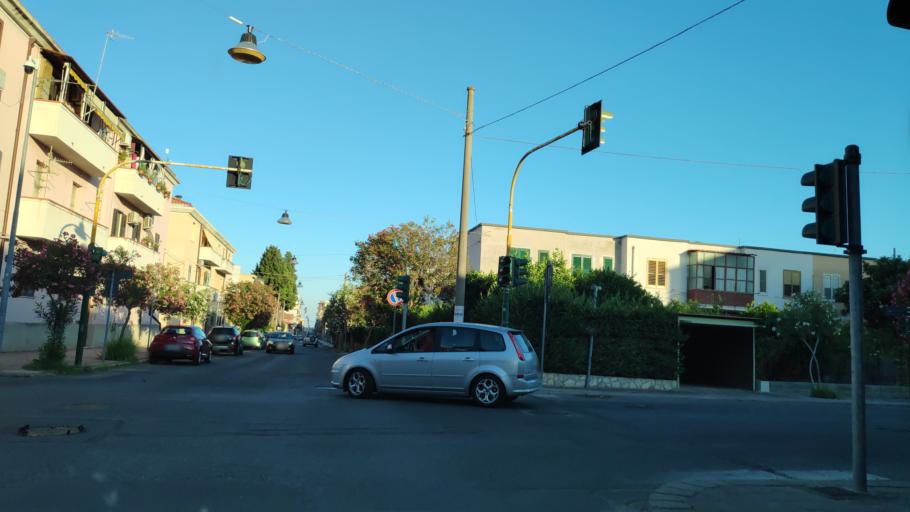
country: IT
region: Calabria
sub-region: Provincia di Reggio Calabria
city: Locri
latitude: 38.2368
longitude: 16.2588
